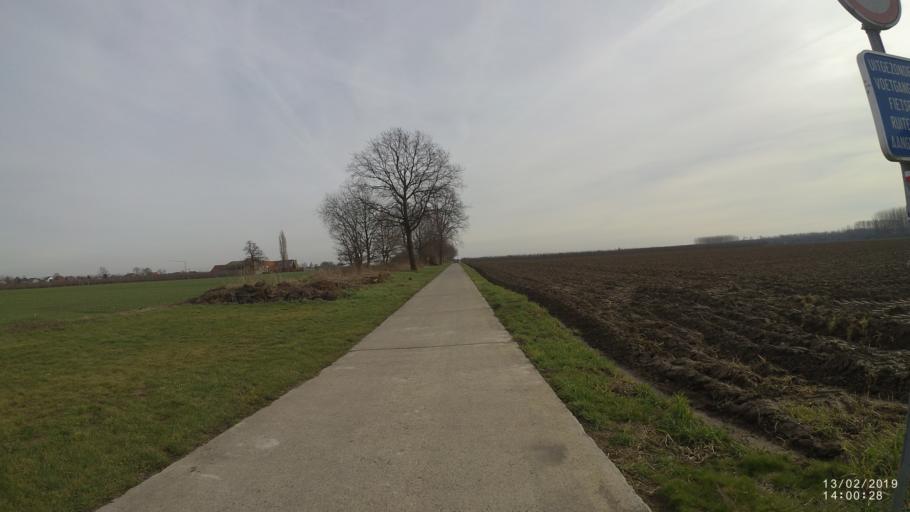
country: BE
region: Flanders
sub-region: Provincie Vlaams-Brabant
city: Zoutleeuw
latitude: 50.8206
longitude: 5.1246
